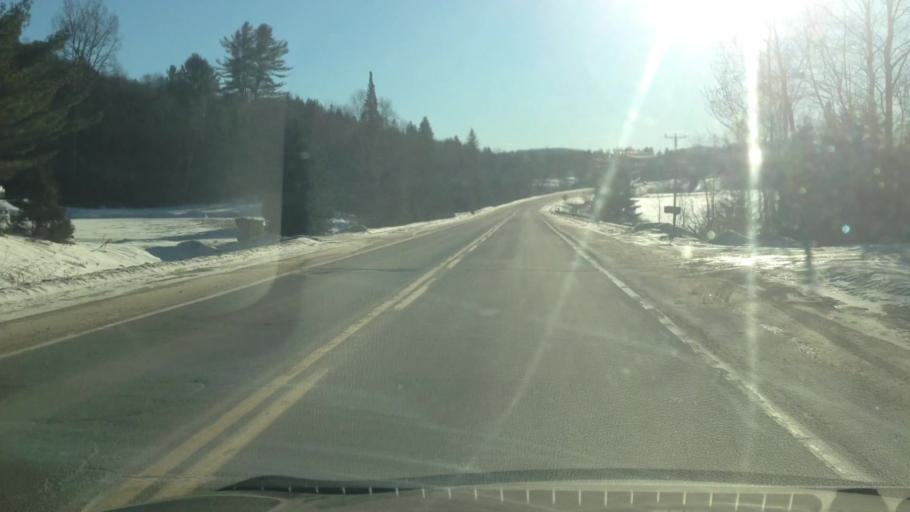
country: CA
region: Quebec
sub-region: Laurentides
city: Mont-Tremblant
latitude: 46.1038
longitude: -74.6025
